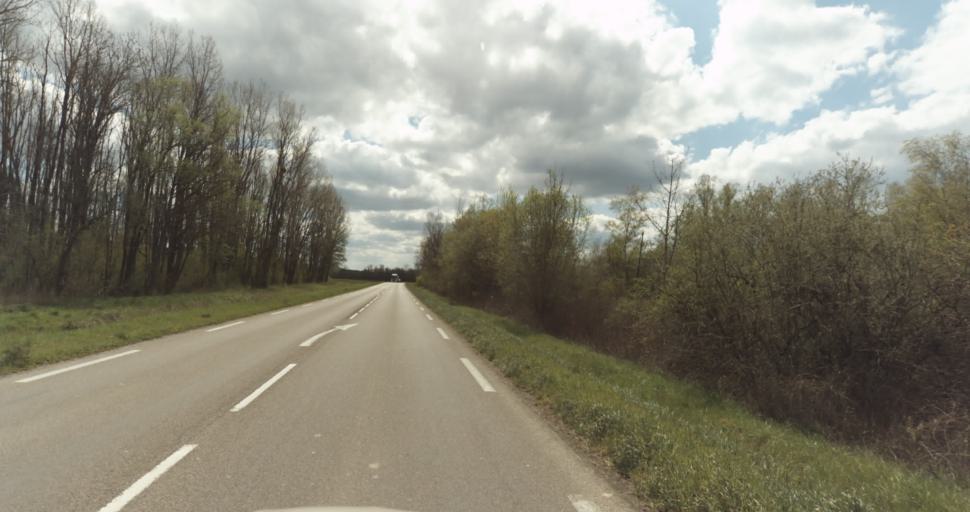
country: FR
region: Bourgogne
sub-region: Departement de la Cote-d'Or
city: Auxonne
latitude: 47.1692
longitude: 5.4026
